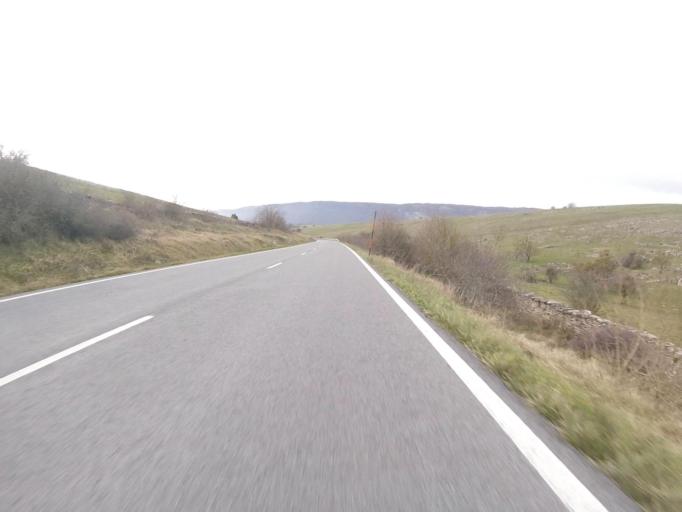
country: ES
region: Navarre
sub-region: Provincia de Navarra
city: Arbizu
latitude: 42.8518
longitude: -2.0155
